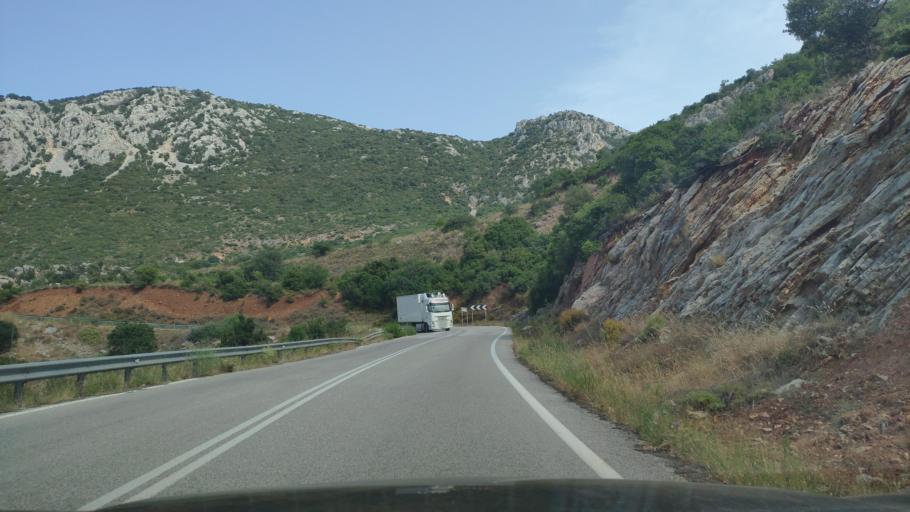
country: GR
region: Peloponnese
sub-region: Nomos Argolidos
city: Palaia Epidavros
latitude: 37.6021
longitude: 23.1621
